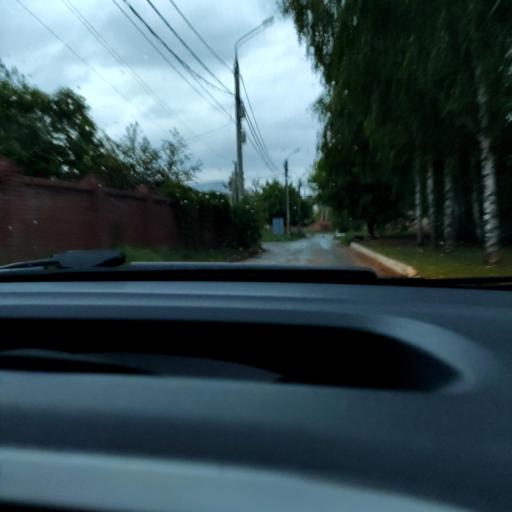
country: RU
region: Samara
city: Tol'yatti
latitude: 53.5425
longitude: 49.3740
